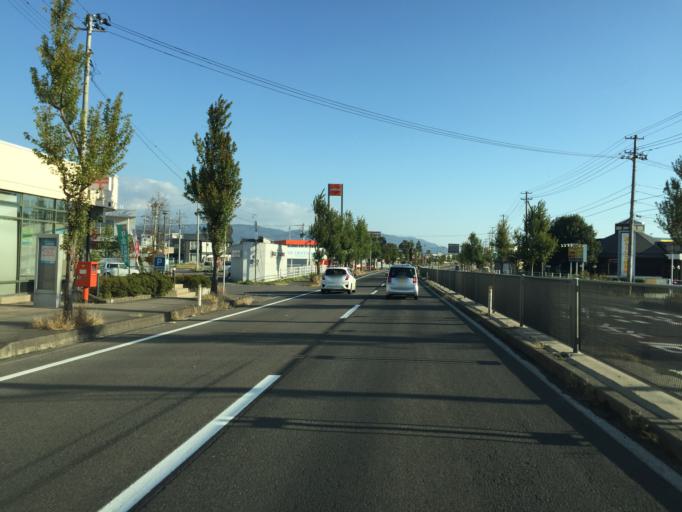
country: JP
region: Fukushima
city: Hobaramachi
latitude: 37.8214
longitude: 140.5056
